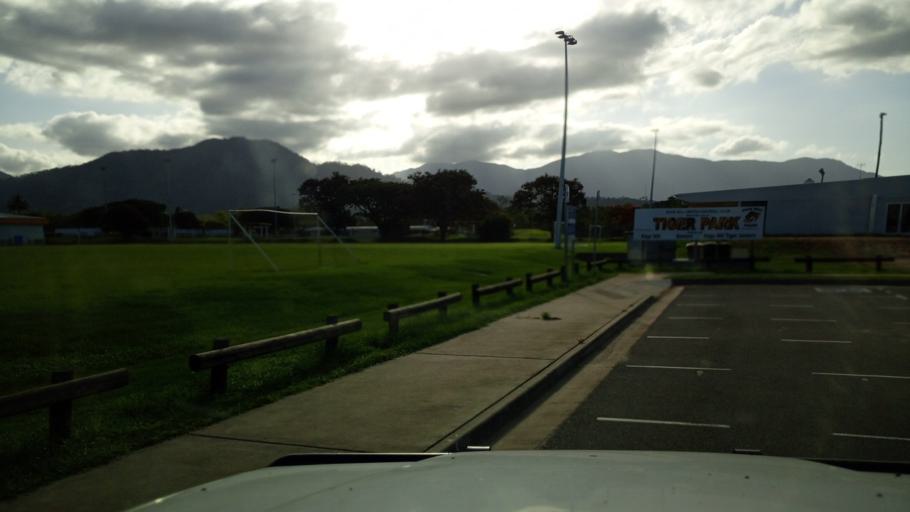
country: AU
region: Queensland
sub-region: Cairns
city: Cairns
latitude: -16.9058
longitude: 145.7493
